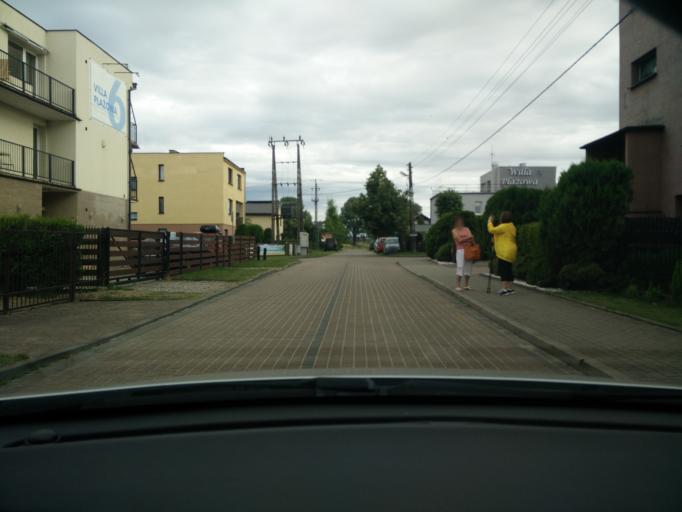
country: PL
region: Pomeranian Voivodeship
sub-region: Powiat pucki
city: Mosty
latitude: 54.6309
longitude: 18.5041
